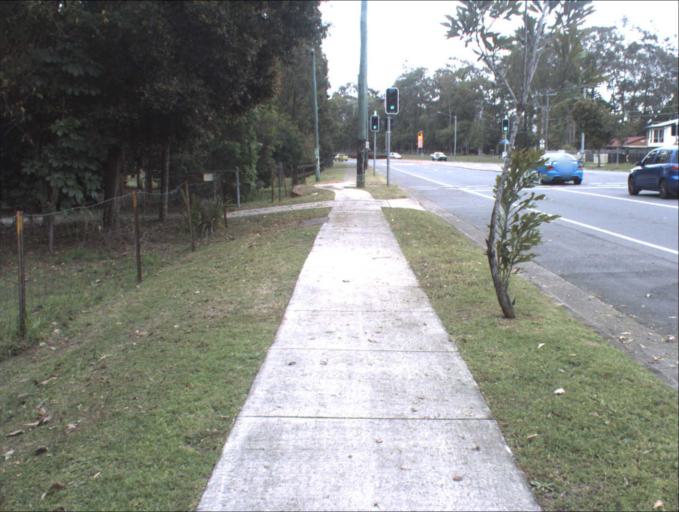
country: AU
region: Queensland
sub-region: Logan
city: Park Ridge South
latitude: -27.6850
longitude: 153.0148
